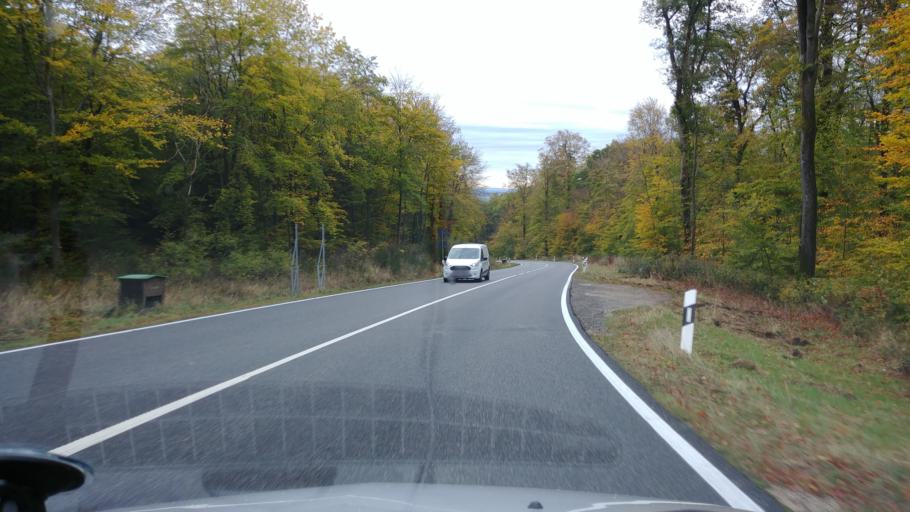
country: DE
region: Hesse
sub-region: Regierungsbezirk Darmstadt
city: Bad Schwalbach
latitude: 50.1275
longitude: 8.0508
